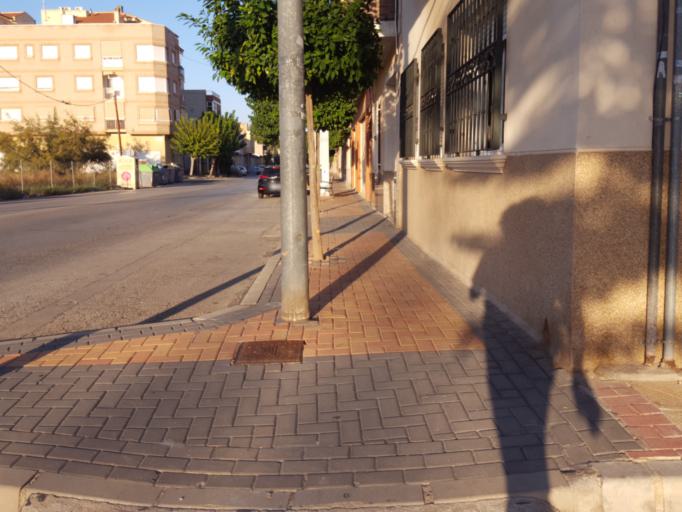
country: ES
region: Murcia
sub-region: Murcia
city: Murcia
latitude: 38.0066
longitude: -1.1619
